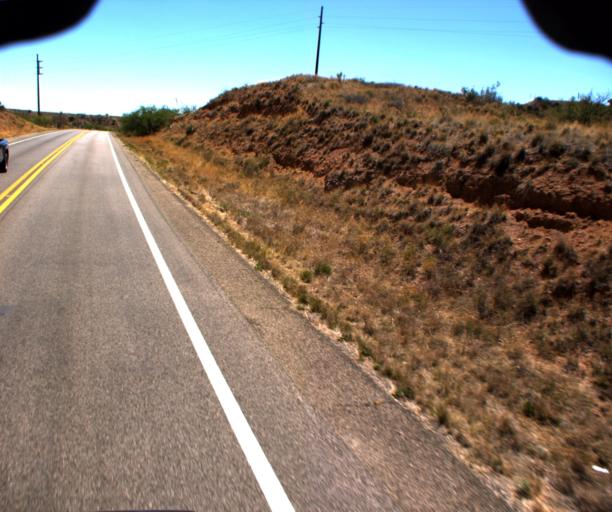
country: US
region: Arizona
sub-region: Pima County
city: Corona de Tucson
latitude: 31.7249
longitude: -110.6567
